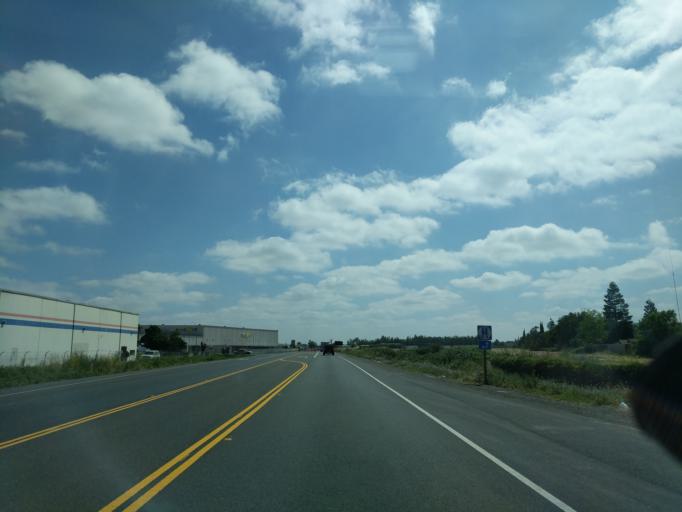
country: US
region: California
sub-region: San Joaquin County
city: Country Club
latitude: 37.9295
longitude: -121.3248
